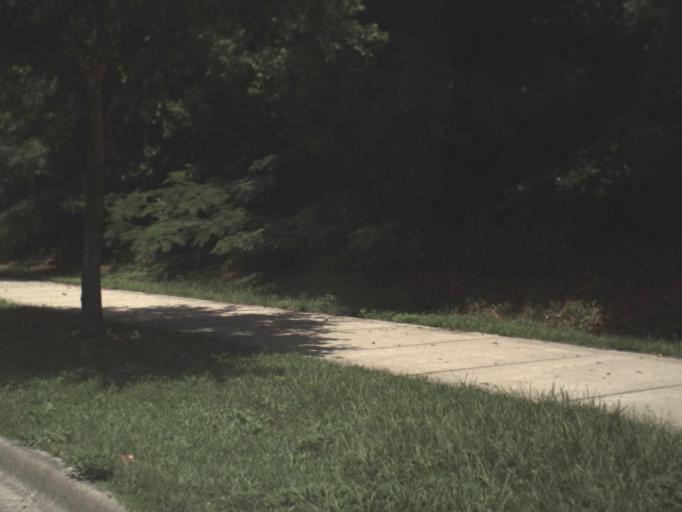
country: US
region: Florida
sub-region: Alachua County
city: Gainesville
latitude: 29.6505
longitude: -82.3644
